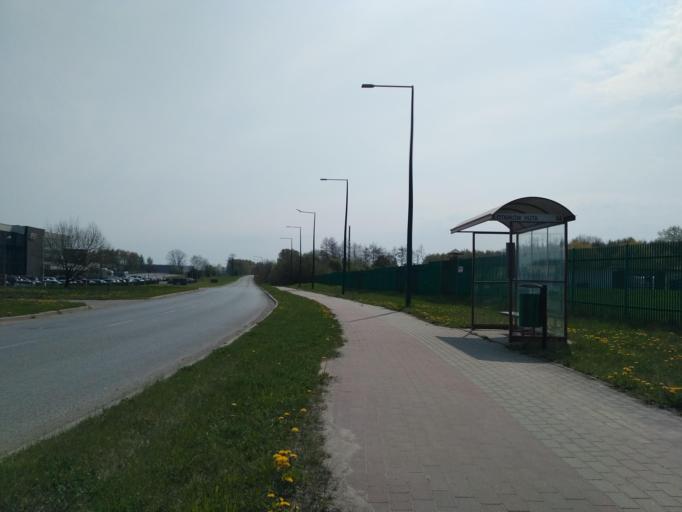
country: PL
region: Subcarpathian Voivodeship
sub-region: Krosno
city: Krosno
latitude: 49.6771
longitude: 21.7289
